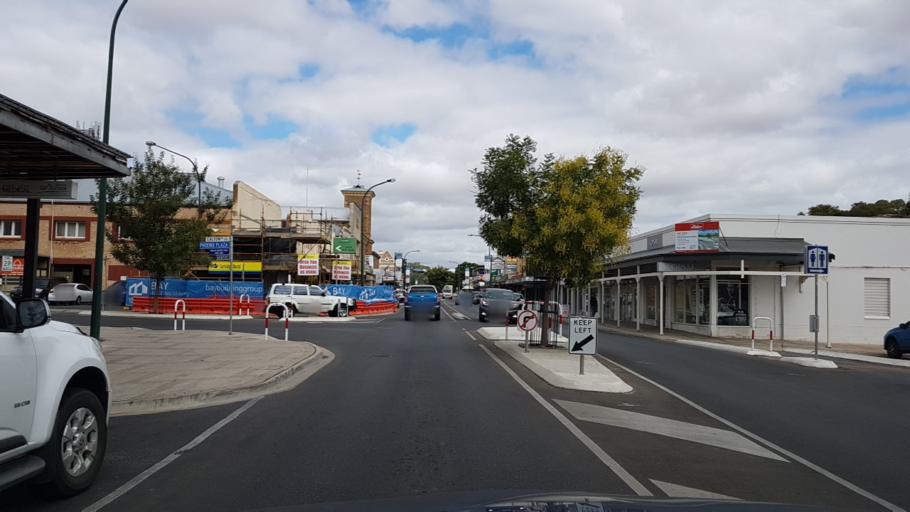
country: AU
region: South Australia
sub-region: Gawler
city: Gawler
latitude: -34.5999
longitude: 138.7492
